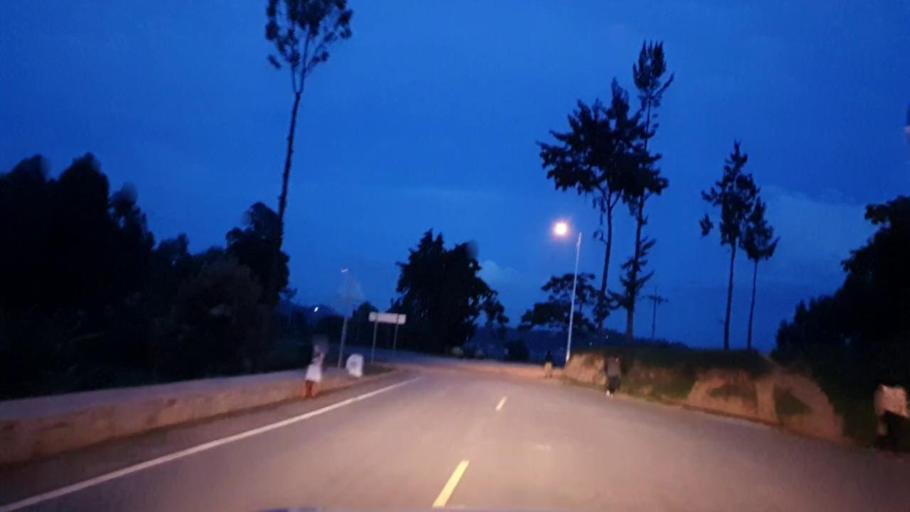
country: RW
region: Southern Province
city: Gikongoro
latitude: -2.4653
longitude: 29.5746
